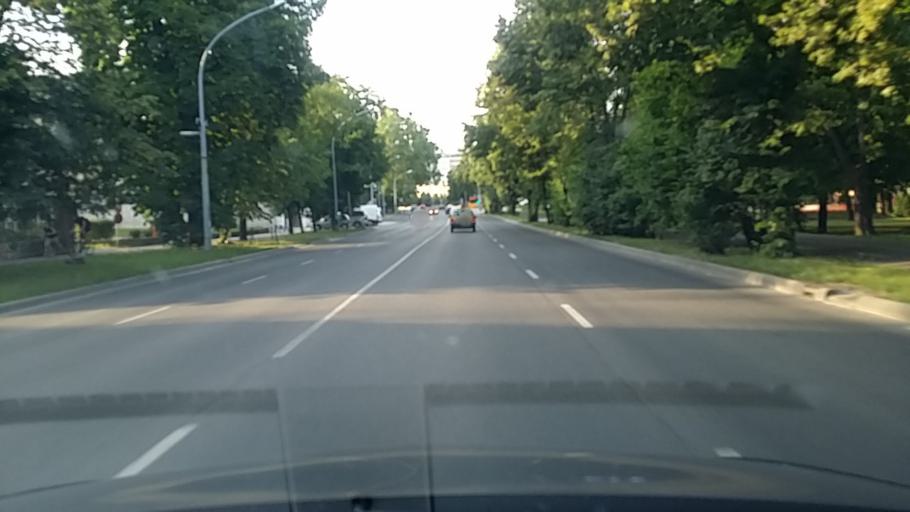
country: HU
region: Borsod-Abauj-Zemplen
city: Miskolc
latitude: 48.0949
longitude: 20.7857
